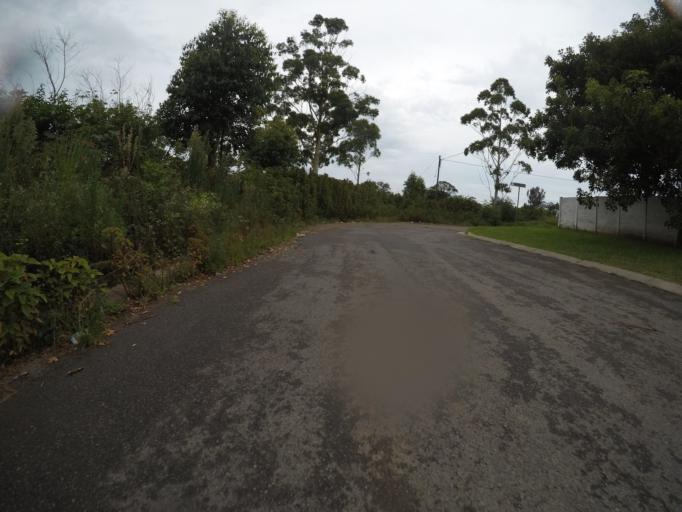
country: ZA
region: Eastern Cape
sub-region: Buffalo City Metropolitan Municipality
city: East London
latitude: -32.9672
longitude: 27.8365
